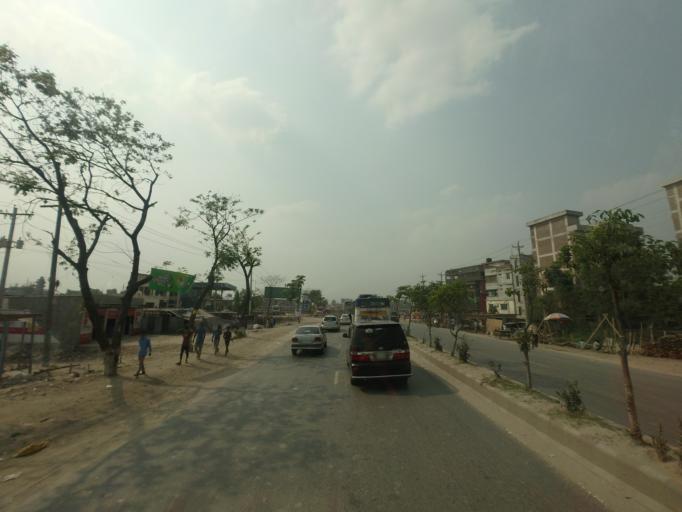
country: BD
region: Dhaka
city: Azimpur
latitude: 23.7876
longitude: 90.3276
